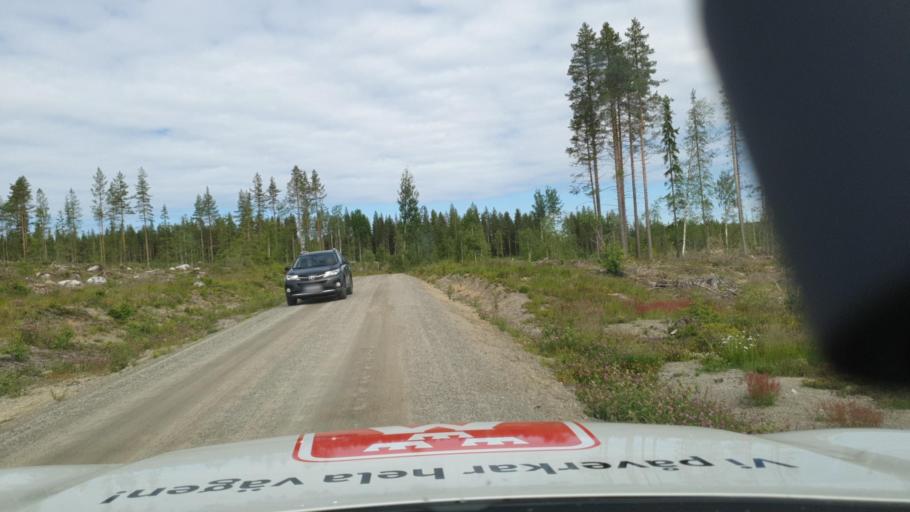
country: SE
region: Vaesterbotten
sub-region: Skelleftea Kommun
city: Langsele
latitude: 64.5599
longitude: 20.2910
